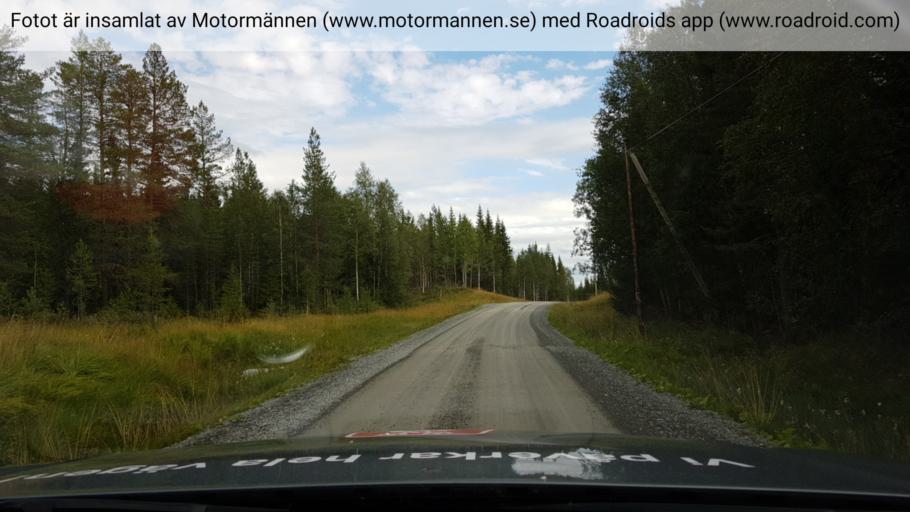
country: SE
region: Jaemtland
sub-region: Krokoms Kommun
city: Valla
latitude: 63.7103
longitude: 13.5459
